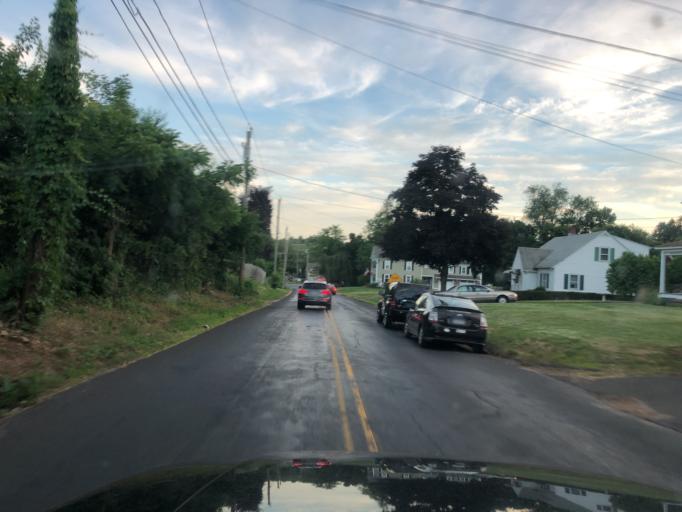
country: US
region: Connecticut
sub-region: Middlesex County
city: Durham
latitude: 41.5294
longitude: -72.6984
